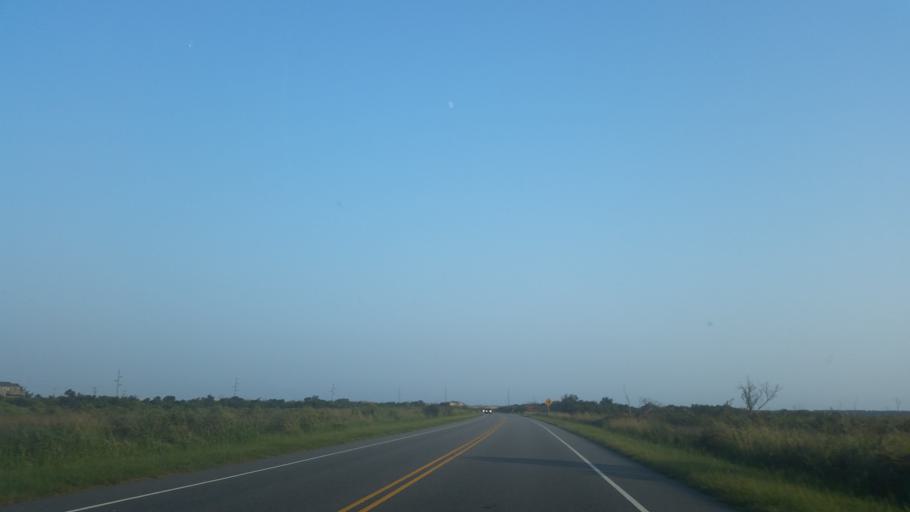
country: US
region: North Carolina
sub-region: Dare County
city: Wanchese
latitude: 35.8472
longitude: -75.5694
